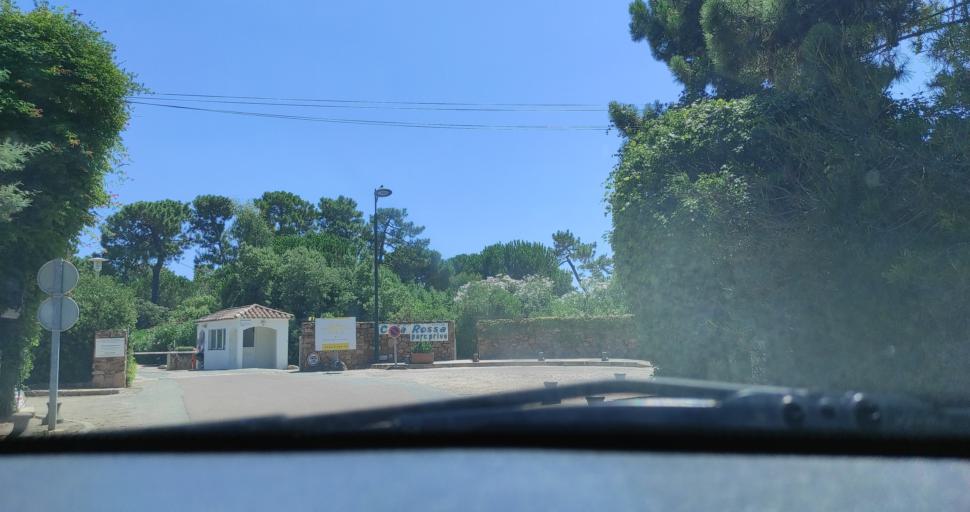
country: FR
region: Corsica
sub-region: Departement de la Corse-du-Sud
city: Porto-Vecchio
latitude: 41.6227
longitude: 9.3360
